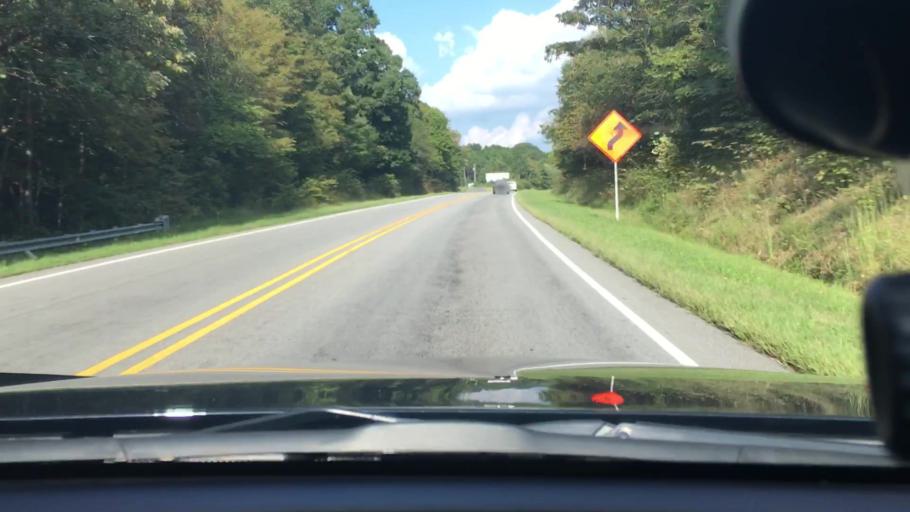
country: US
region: North Carolina
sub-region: Randolph County
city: Asheboro
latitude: 35.6718
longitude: -79.8723
